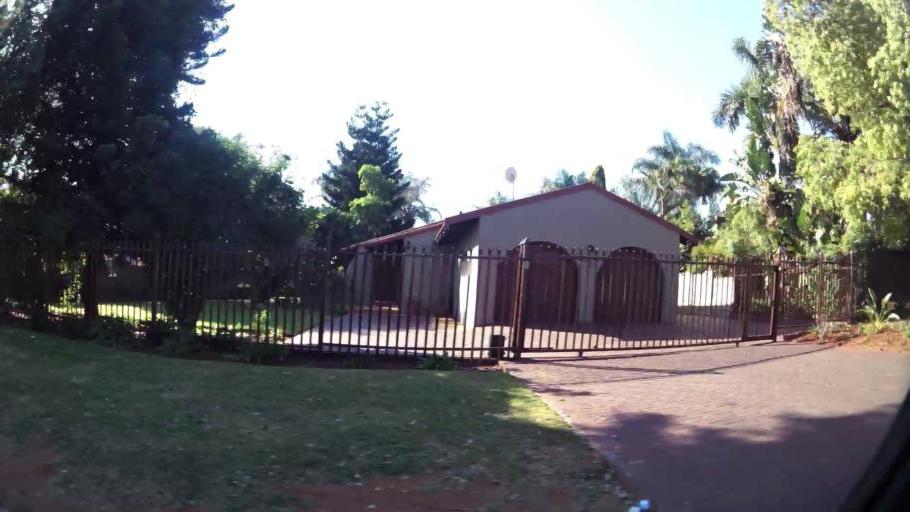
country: ZA
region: Gauteng
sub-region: City of Tshwane Metropolitan Municipality
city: Pretoria
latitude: -25.6687
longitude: 28.1431
